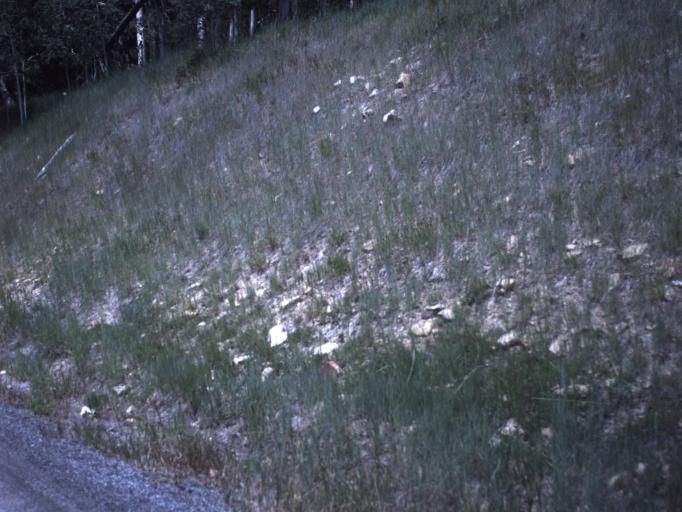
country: US
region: Utah
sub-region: Sanpete County
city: Fairview
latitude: 39.6806
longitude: -111.2259
